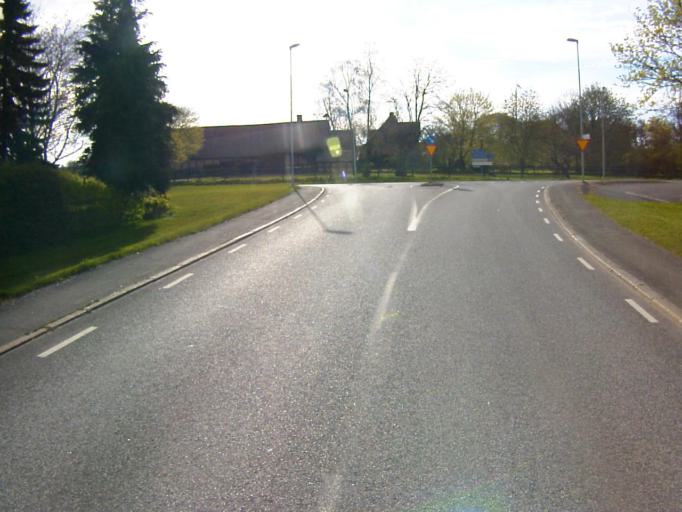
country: SE
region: Skane
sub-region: Kristianstads Kommun
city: Norra Asum
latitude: 55.9899
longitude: 14.1521
